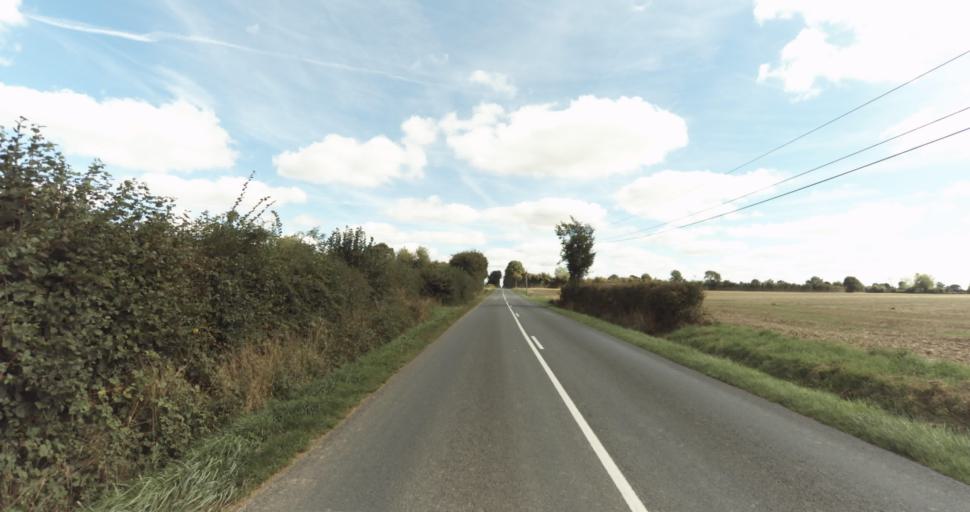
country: FR
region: Lower Normandy
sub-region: Departement de l'Orne
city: Gace
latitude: 48.8980
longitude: 0.3152
